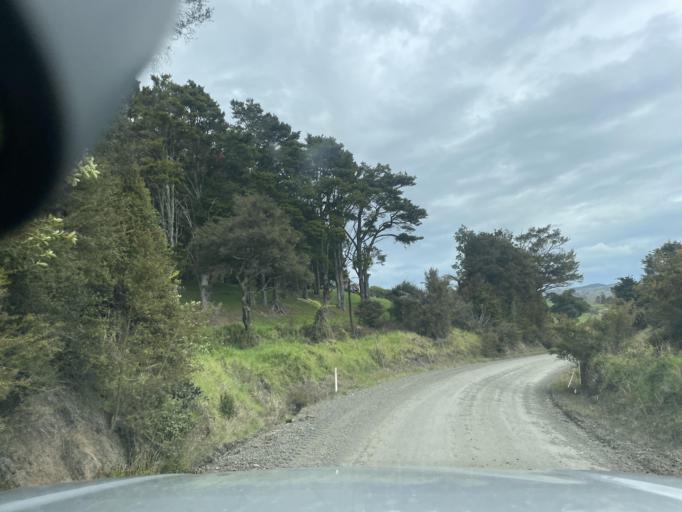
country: NZ
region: Northland
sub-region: Kaipara District
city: Dargaville
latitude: -35.8218
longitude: 173.7925
